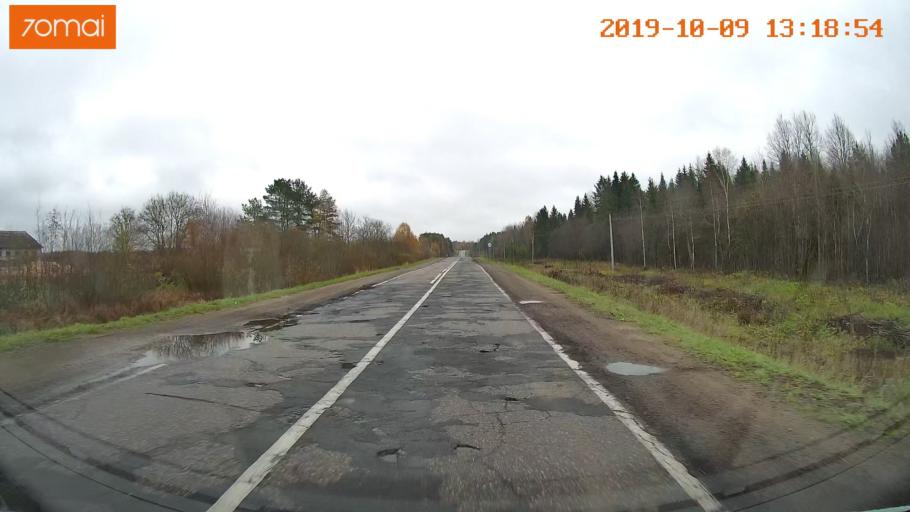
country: RU
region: Jaroslavl
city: Lyubim
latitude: 58.3501
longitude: 40.8033
